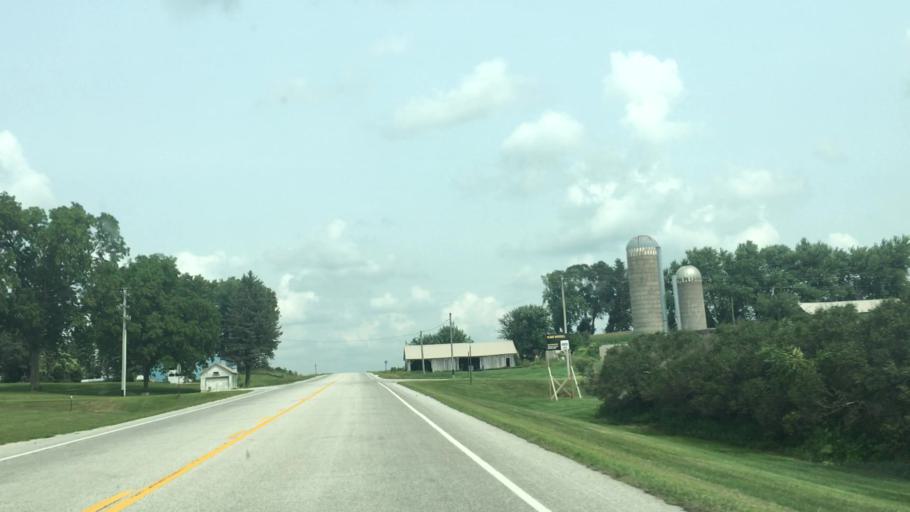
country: US
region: Minnesota
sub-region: Fillmore County
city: Harmony
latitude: 43.6155
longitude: -91.9298
